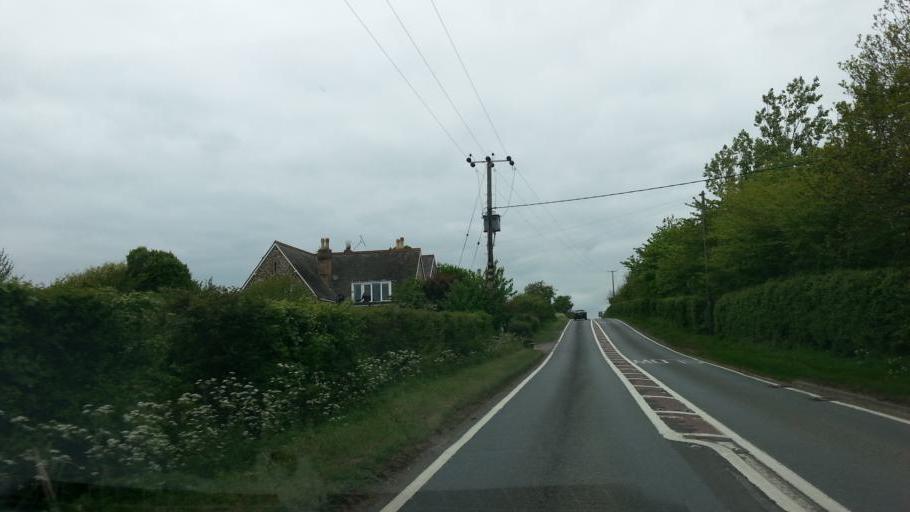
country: GB
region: England
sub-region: Suffolk
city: Bury St Edmunds
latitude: 52.2615
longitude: 0.6780
